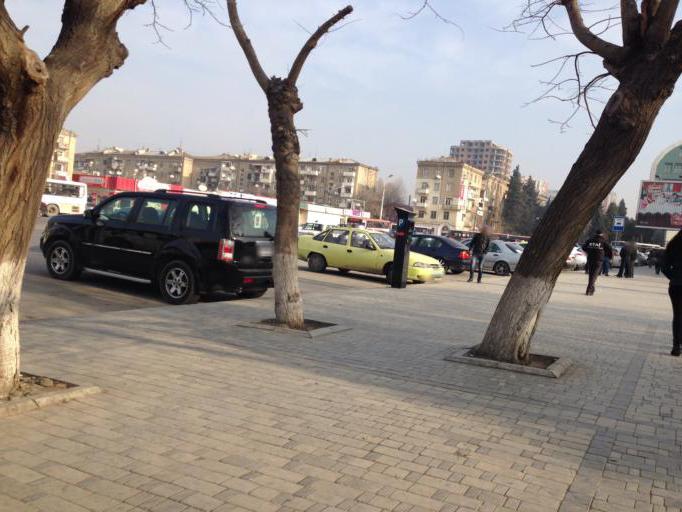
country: AZ
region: Baki
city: Baku
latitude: 40.4024
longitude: 49.8705
